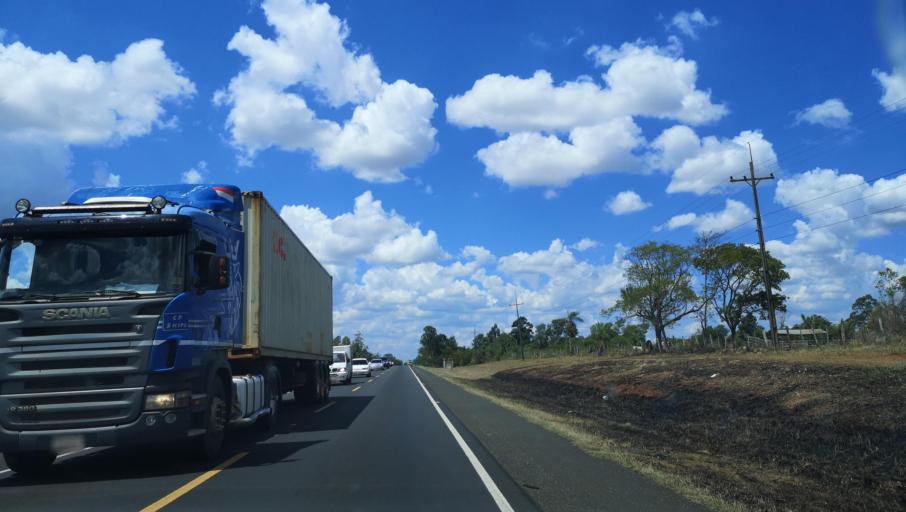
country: PY
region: Itapua
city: General Delgado
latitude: -27.0747
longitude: -56.5895
